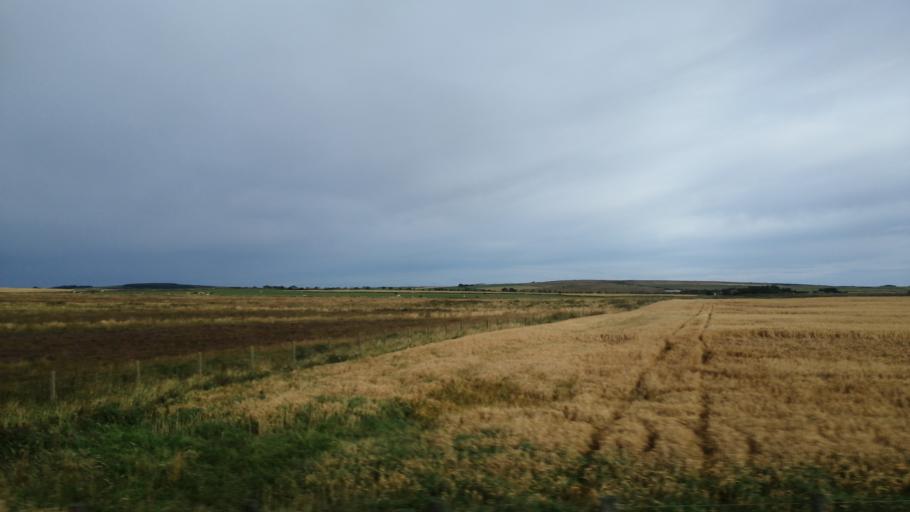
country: GB
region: Scotland
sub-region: Highland
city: Thurso
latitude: 58.5014
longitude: -3.5032
